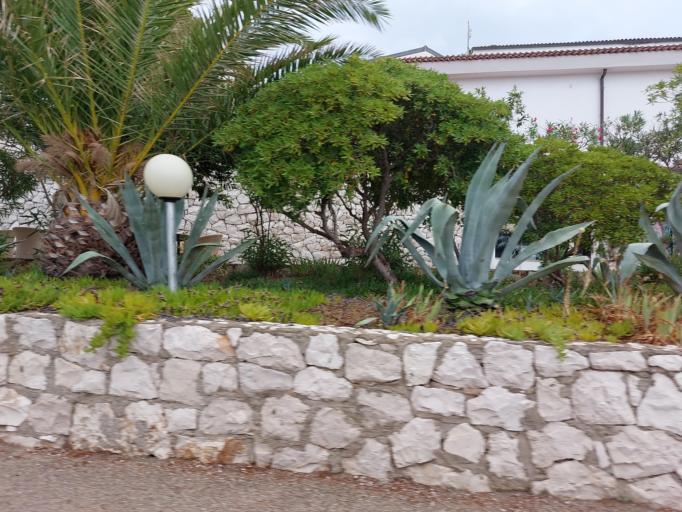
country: HR
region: Dubrovacko-Neretvanska
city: Smokvica
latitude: 42.7658
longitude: 16.8225
